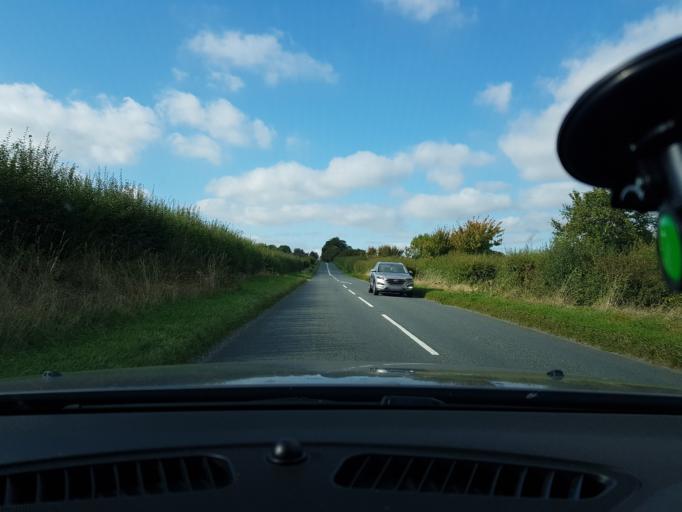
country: GB
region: England
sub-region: Wiltshire
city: Aldbourne
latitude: 51.4938
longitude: -1.6495
